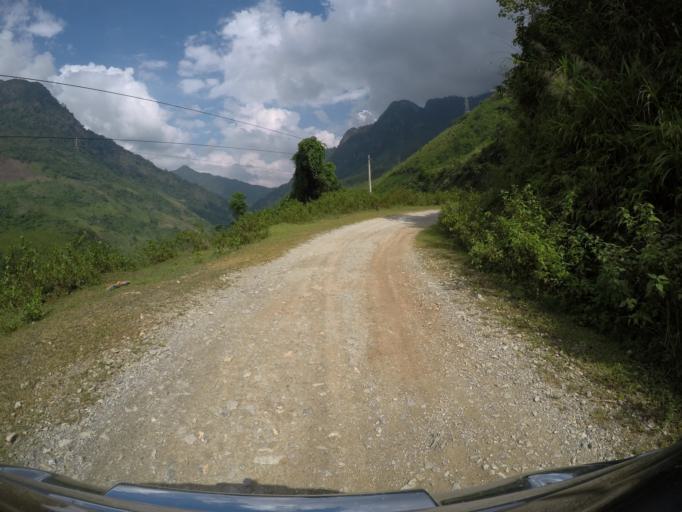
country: VN
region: Yen Bai
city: Son Thinh
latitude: 21.6791
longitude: 104.5496
